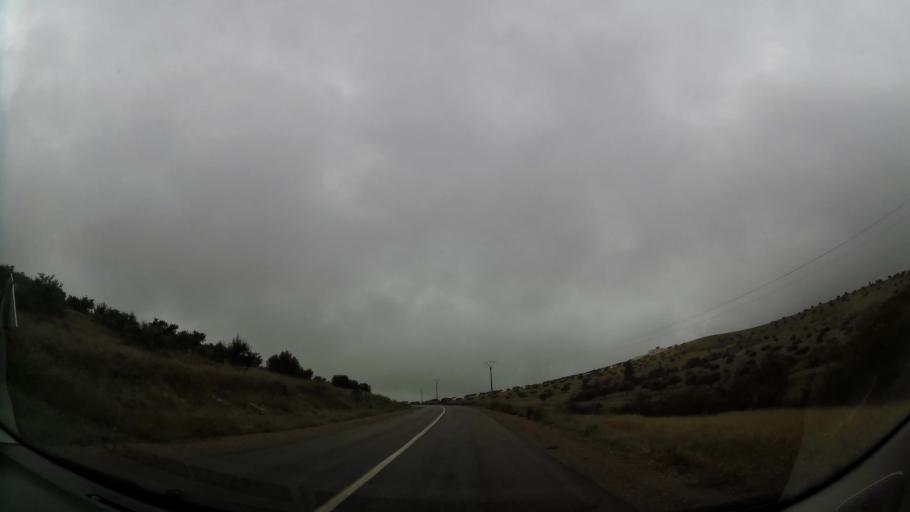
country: MA
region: Oriental
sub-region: Nador
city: Selouane
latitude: 35.1220
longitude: -3.0622
